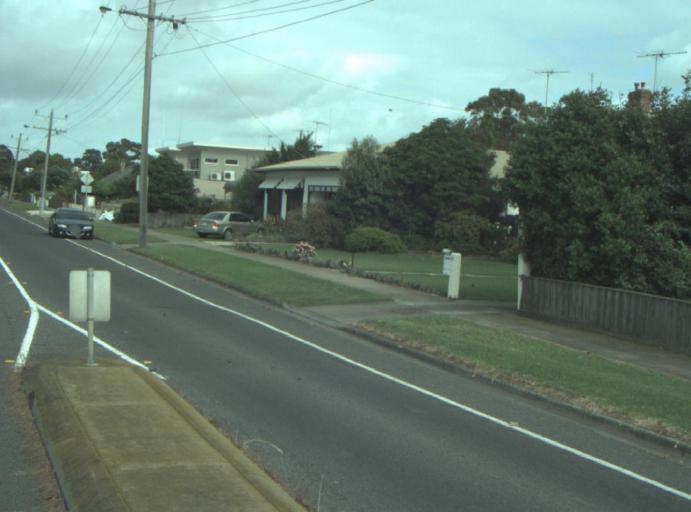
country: AU
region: Victoria
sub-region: Greater Geelong
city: Bell Park
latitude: -38.1008
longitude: 144.3757
